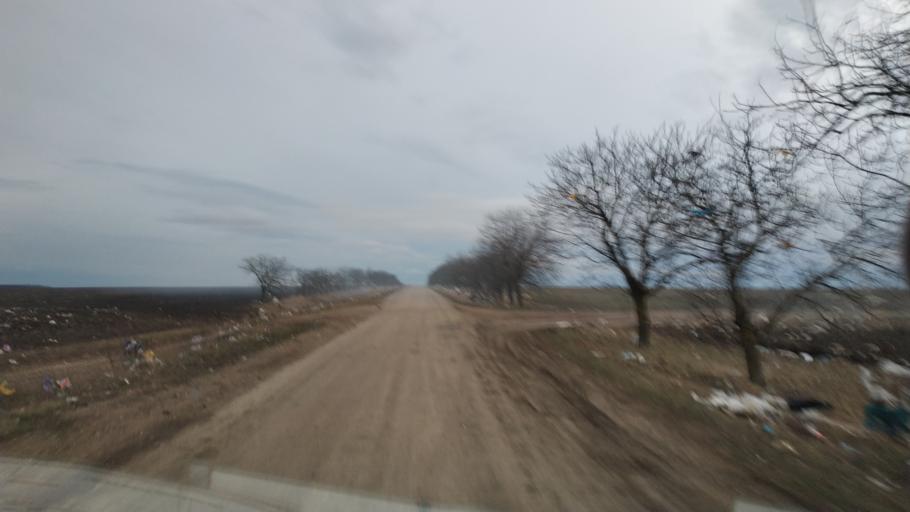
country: MD
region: Causeni
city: Causeni
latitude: 46.5907
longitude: 29.3952
